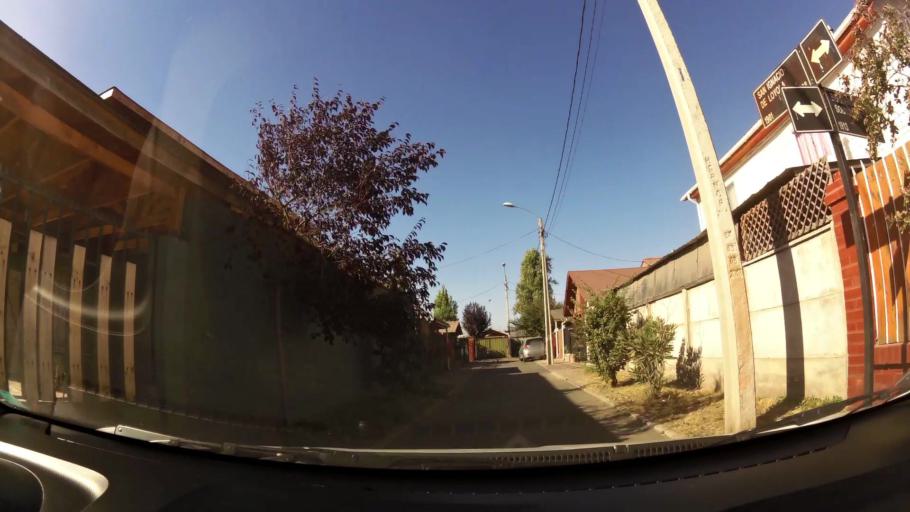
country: CL
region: O'Higgins
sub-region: Provincia de Cachapoal
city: Rancagua
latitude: -34.1803
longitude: -70.7612
